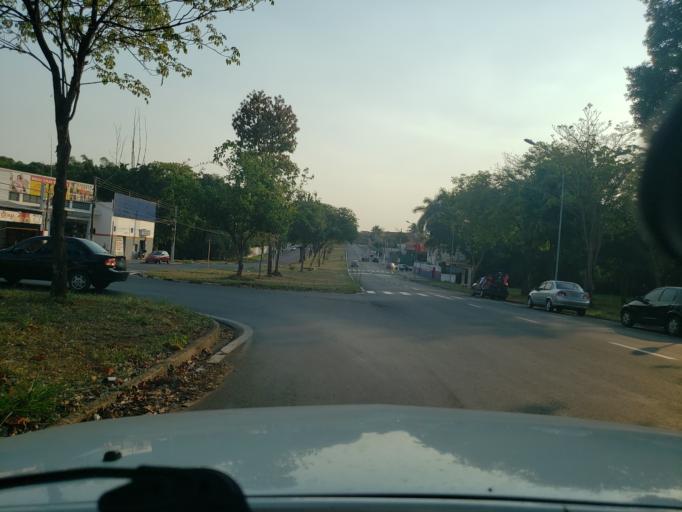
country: BR
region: Sao Paulo
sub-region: Moji-Guacu
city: Mogi-Gaucu
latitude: -22.3592
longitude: -46.9379
